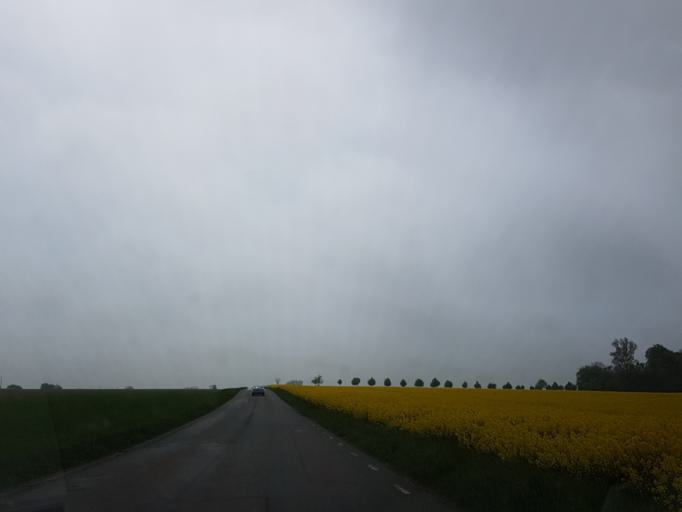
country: SE
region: Skane
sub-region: Tomelilla Kommun
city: Tomelilla
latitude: 55.4700
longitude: 14.0976
